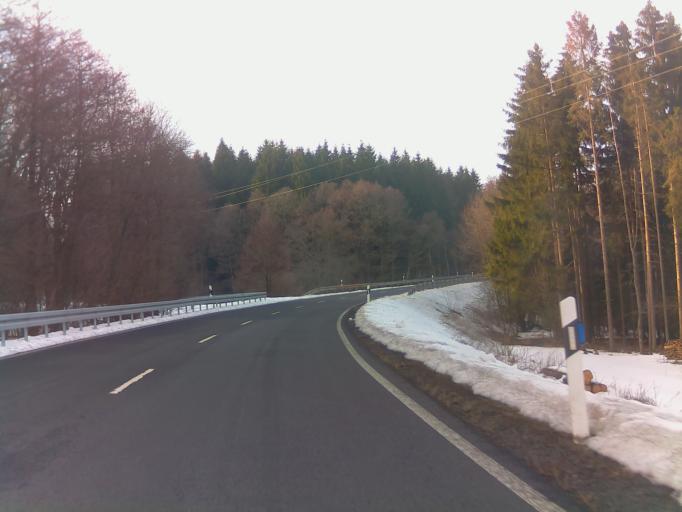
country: DE
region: Bavaria
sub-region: Regierungsbezirk Unterfranken
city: Wildflecken
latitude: 50.3590
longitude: 9.9359
